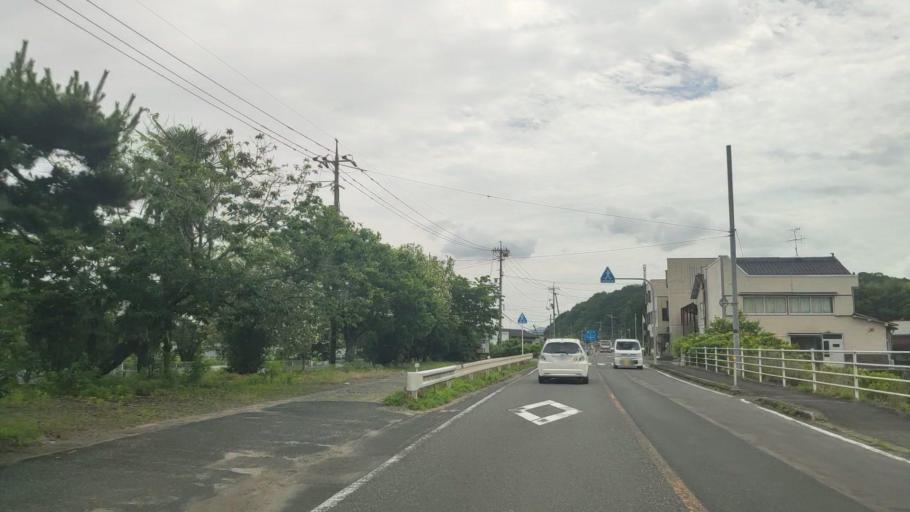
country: JP
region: Okayama
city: Tsuyama
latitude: 35.0594
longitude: 133.8943
